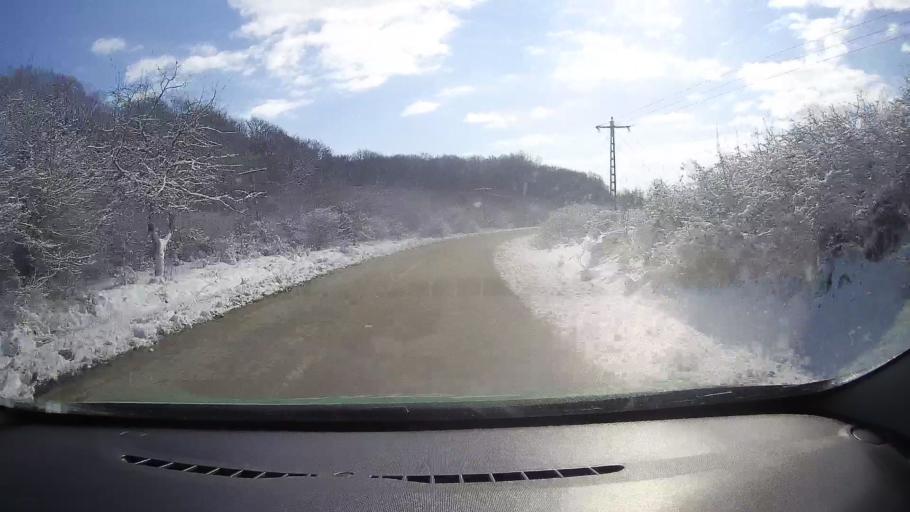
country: RO
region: Sibiu
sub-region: Comuna Altina
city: Altina
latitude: 46.0006
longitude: 24.4272
